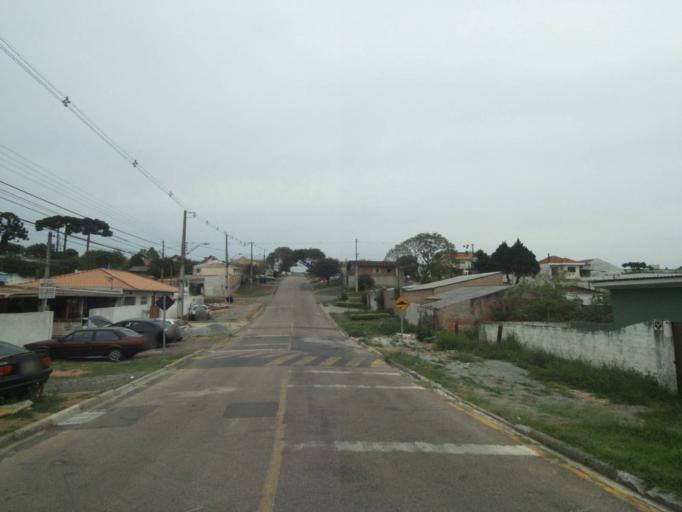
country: BR
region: Parana
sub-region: Pinhais
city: Pinhais
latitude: -25.3964
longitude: -49.1996
